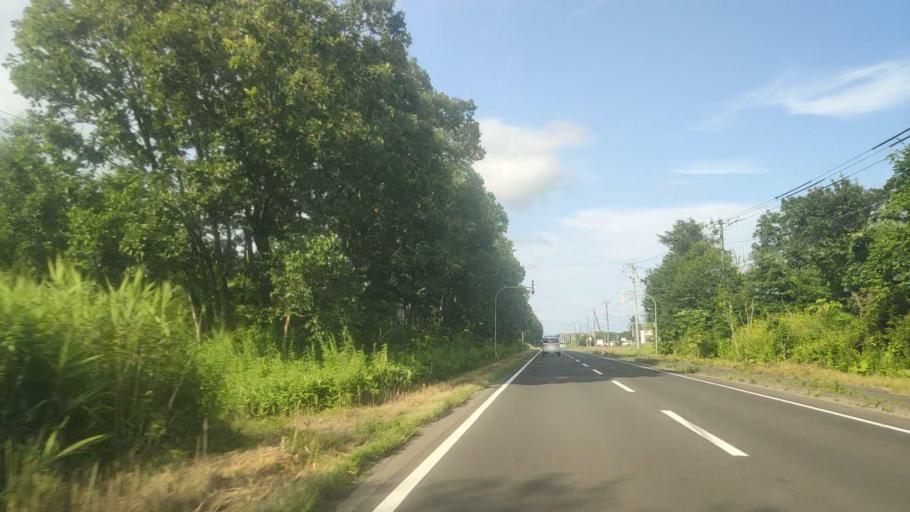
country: JP
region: Hokkaido
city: Chitose
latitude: 42.7400
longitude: 141.7829
